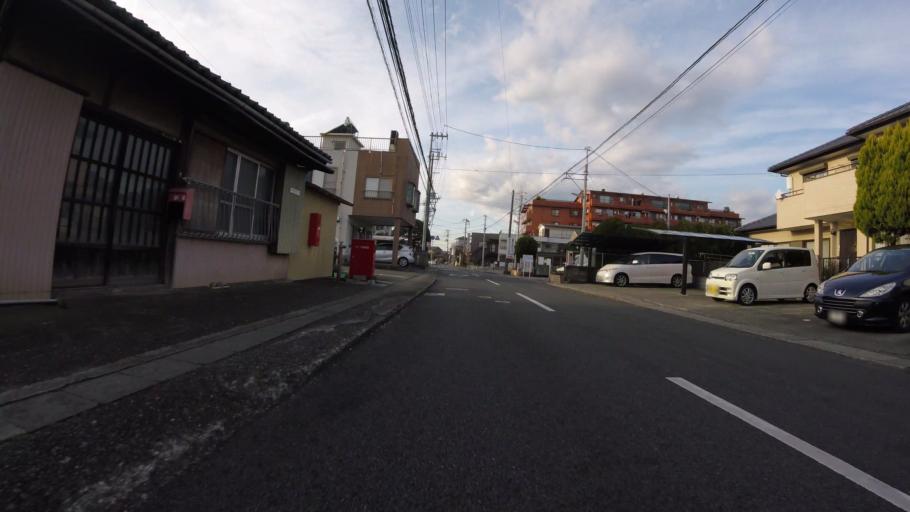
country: JP
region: Shizuoka
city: Mishima
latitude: 35.0897
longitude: 138.9441
